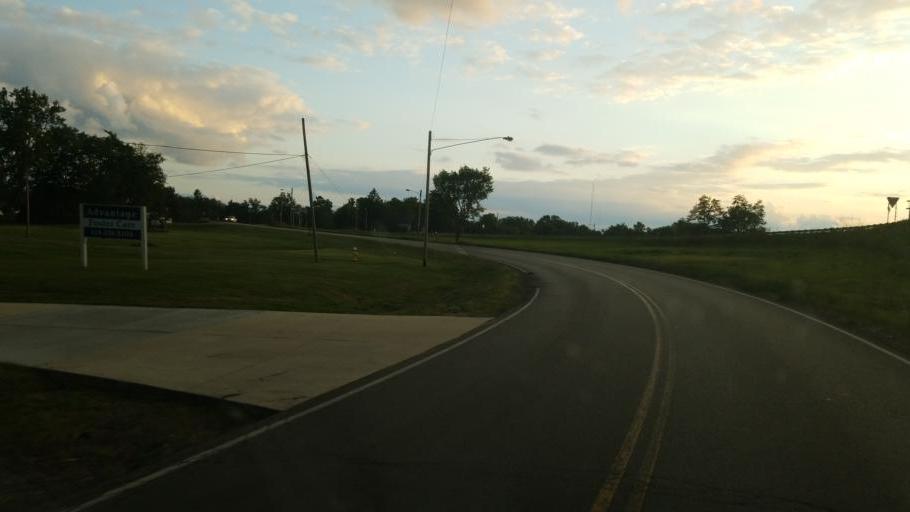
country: US
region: Ohio
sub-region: Richland County
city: Mansfield
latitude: 40.7766
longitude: -82.5305
